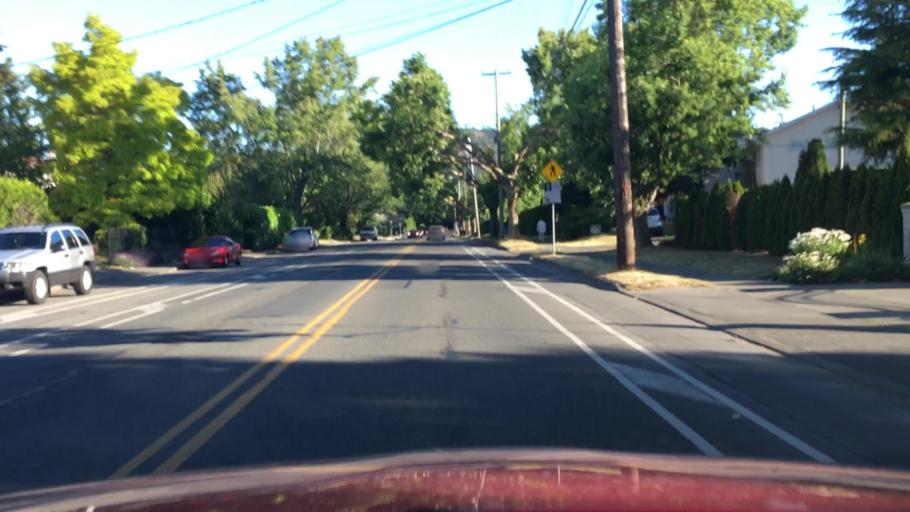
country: CA
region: British Columbia
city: Oak Bay
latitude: 48.4785
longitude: -123.3344
